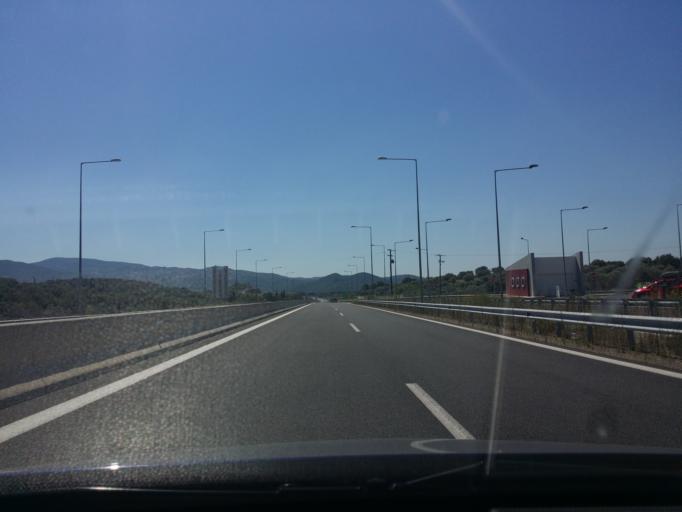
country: GR
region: Peloponnese
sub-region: Nomos Lakonias
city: Magoula
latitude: 37.1967
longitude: 22.3428
